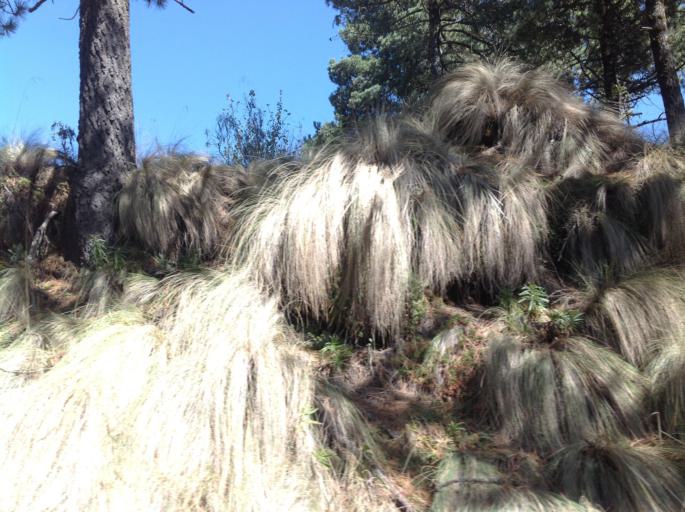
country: MX
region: Mexico
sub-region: Amecameca
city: San Diego Huehuecalco
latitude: 19.0944
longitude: -98.6543
